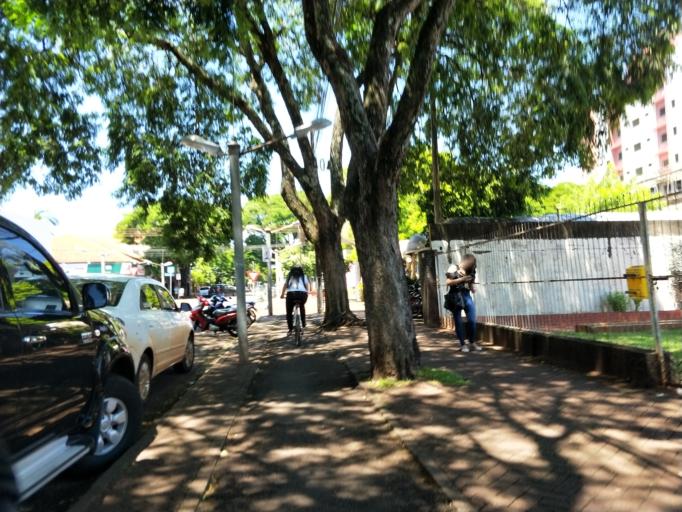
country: BR
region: Parana
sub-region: Marechal Candido Rondon
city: Marechal Candido Rondon
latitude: -24.5609
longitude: -54.0607
